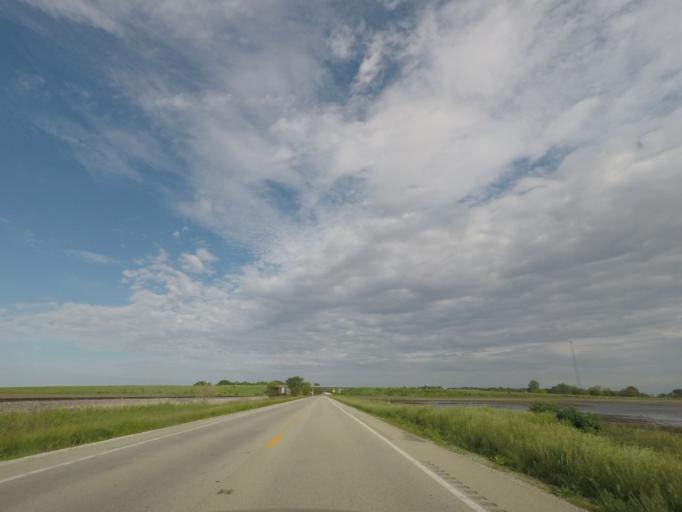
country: US
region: Illinois
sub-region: Logan County
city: Mount Pulaski
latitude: 39.9992
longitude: -89.2683
